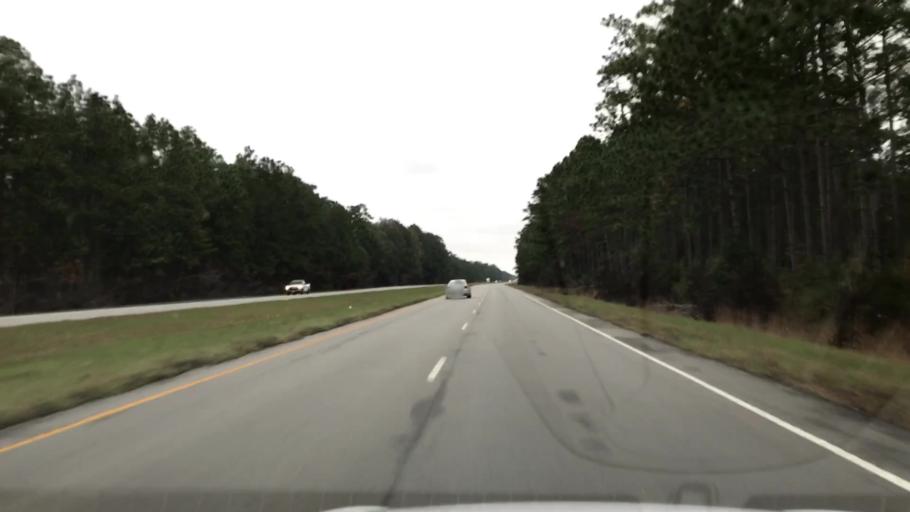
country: US
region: South Carolina
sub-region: Charleston County
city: Awendaw
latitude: 33.1315
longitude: -79.4457
